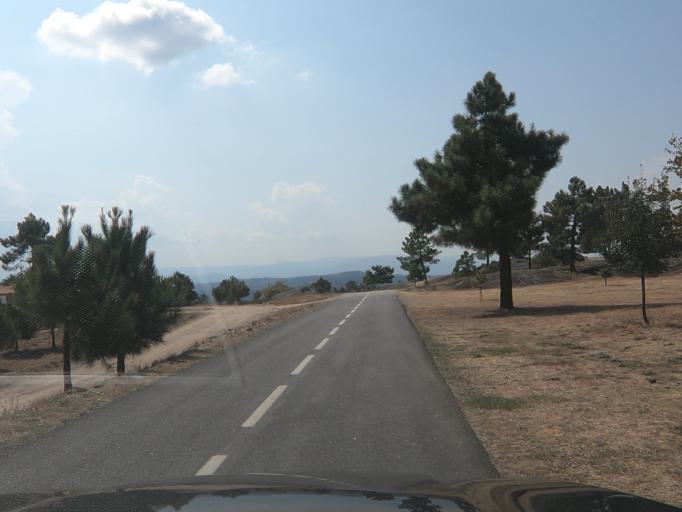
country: PT
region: Vila Real
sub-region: Sabrosa
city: Sabrosa
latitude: 41.2794
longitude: -7.6169
